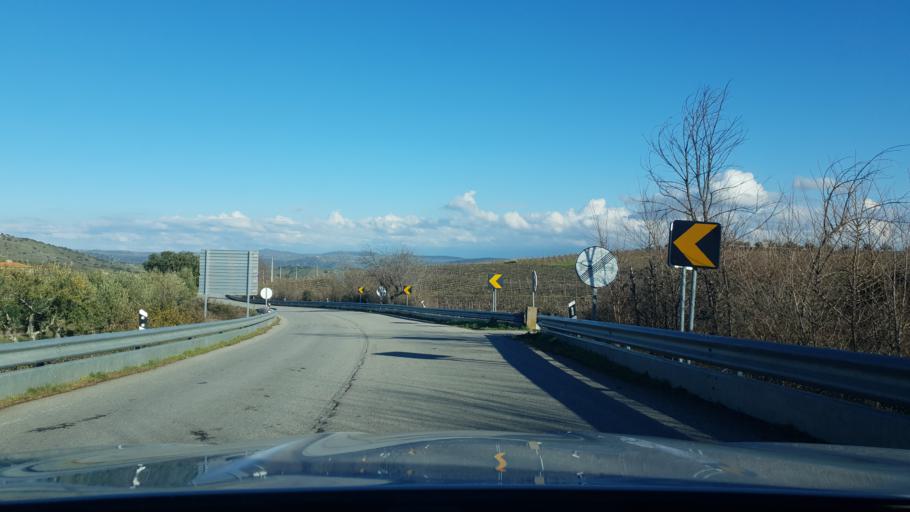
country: PT
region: Braganca
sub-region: Freixo de Espada A Cinta
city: Freixo de Espada a Cinta
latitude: 41.0937
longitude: -6.8305
